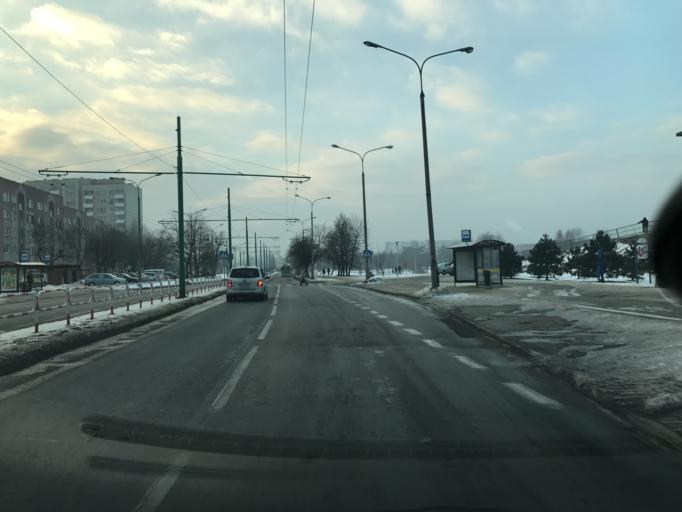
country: PL
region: Silesian Voivodeship
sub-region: Tychy
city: Tychy
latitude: 50.1111
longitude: 18.9751
